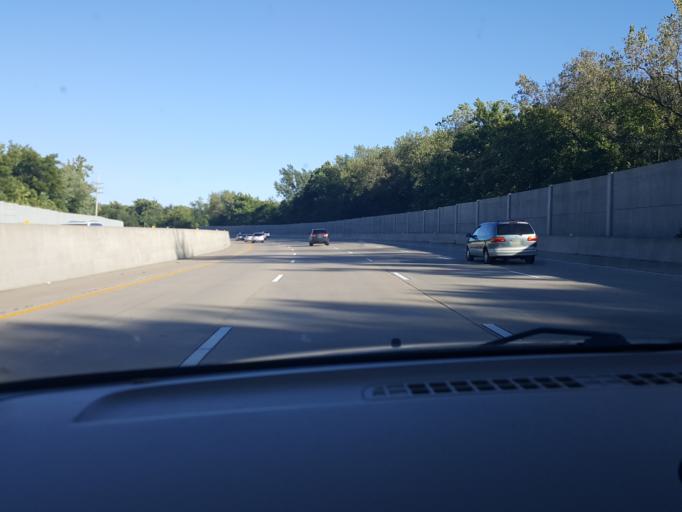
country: US
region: Missouri
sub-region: Saint Louis County
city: Ladue
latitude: 38.6335
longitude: -90.3885
